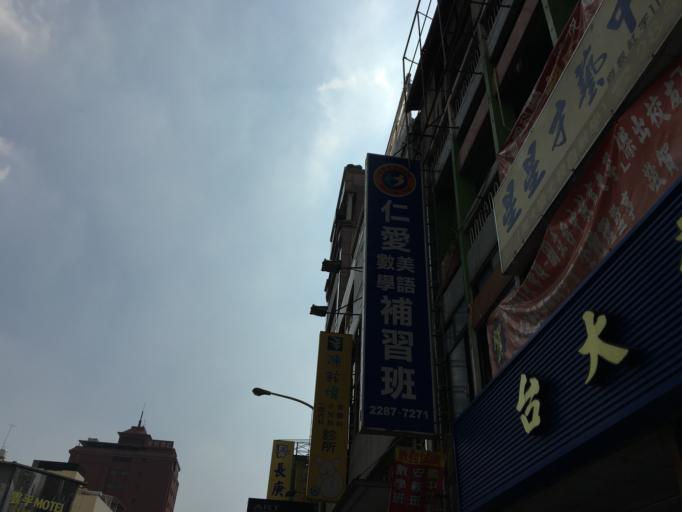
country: TW
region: Taiwan
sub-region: Taichung City
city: Taichung
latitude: 24.1313
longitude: 120.6845
